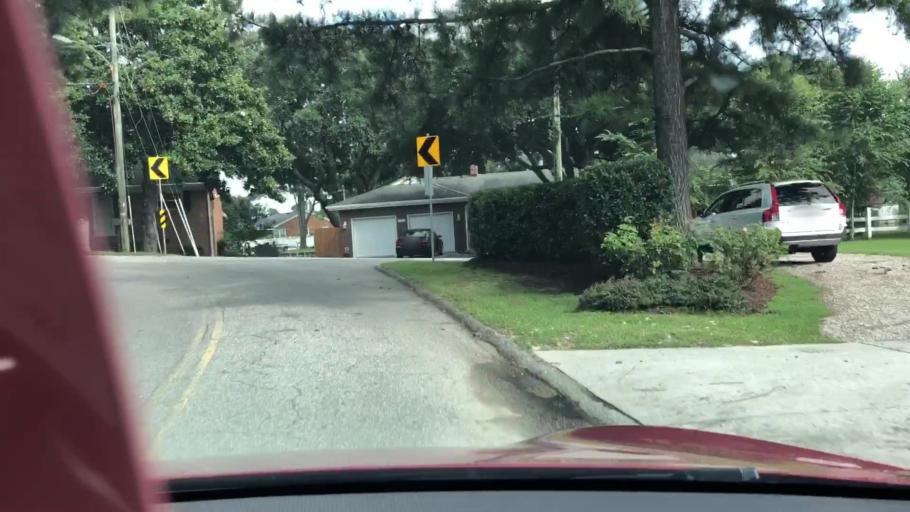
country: US
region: Virginia
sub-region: City of Virginia Beach
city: Virginia Beach
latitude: 36.9063
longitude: -76.0817
